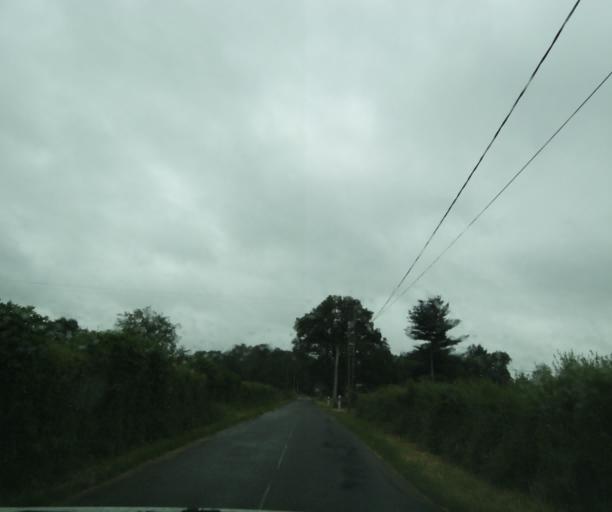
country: FR
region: Bourgogne
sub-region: Departement de Saone-et-Loire
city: Palinges
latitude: 46.5228
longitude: 4.2121
